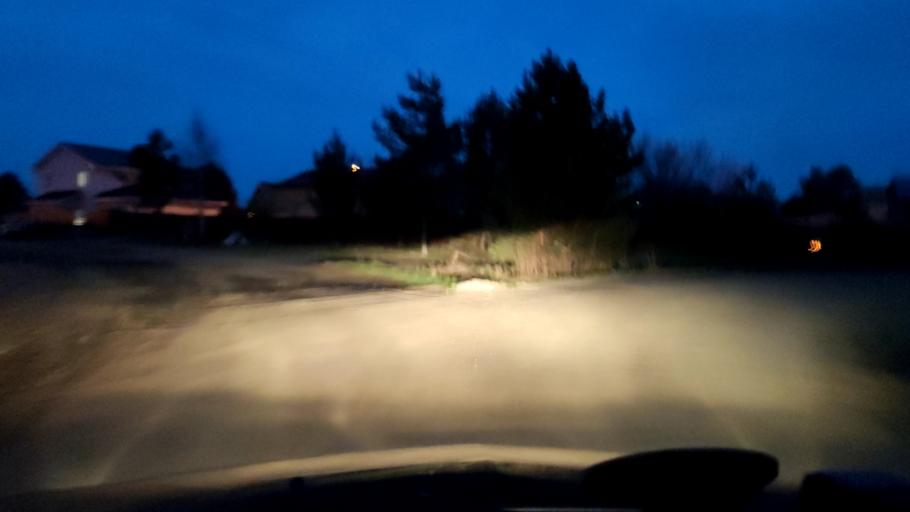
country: RU
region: Voronezj
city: Pridonskoy
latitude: 51.6339
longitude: 39.1095
